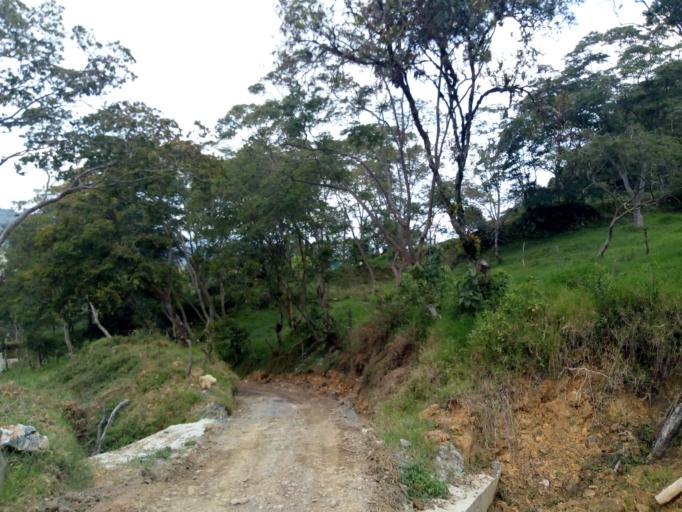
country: CO
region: Boyaca
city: Moniquira
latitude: 5.8655
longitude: -73.5181
